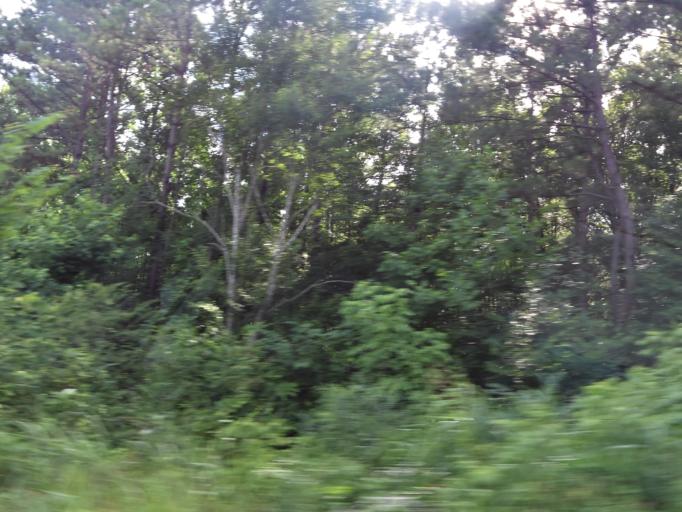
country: US
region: Tennessee
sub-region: Benton County
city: Camden
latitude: 36.0527
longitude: -88.1668
